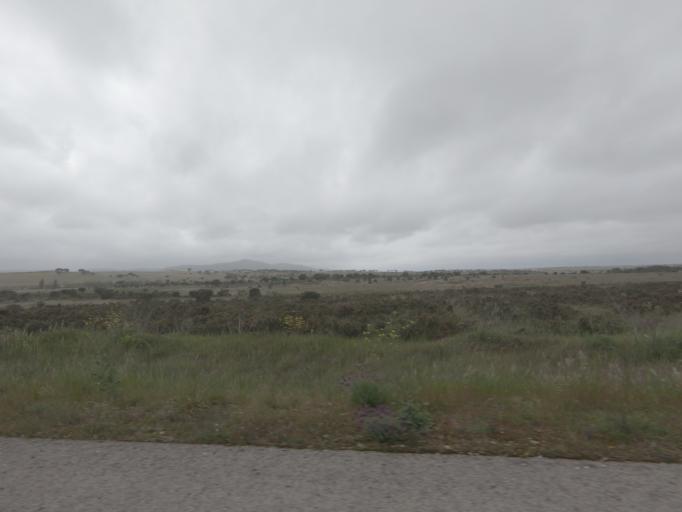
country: ES
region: Extremadura
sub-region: Provincia de Caceres
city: Malpartida de Caceres
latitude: 39.3351
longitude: -6.4828
